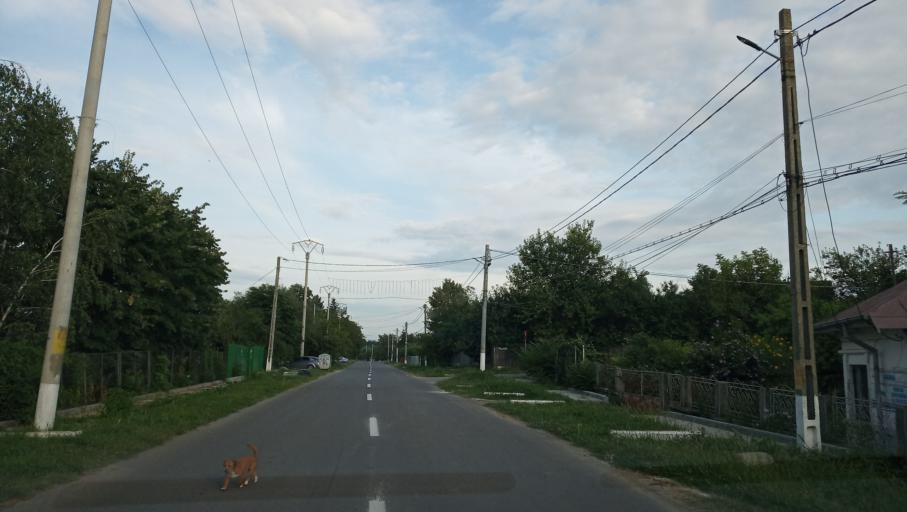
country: RO
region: Giurgiu
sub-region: Comuna Comana
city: Comana
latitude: 44.1716
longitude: 26.1496
